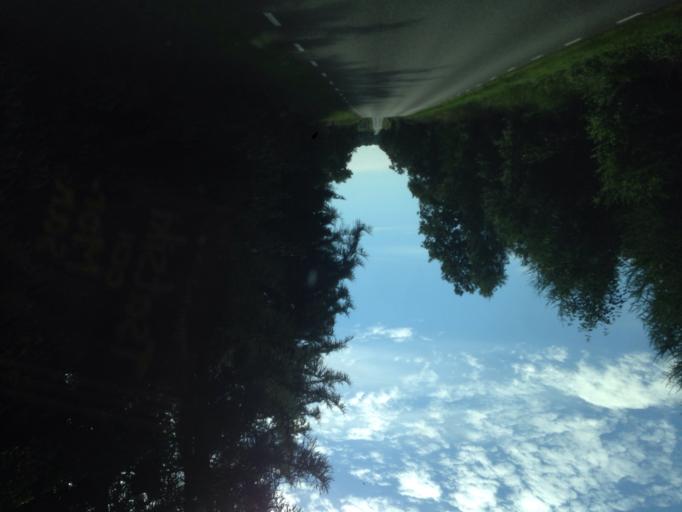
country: SE
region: Skane
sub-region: Tomelilla Kommun
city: Tomelilla
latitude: 55.6391
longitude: 14.0673
